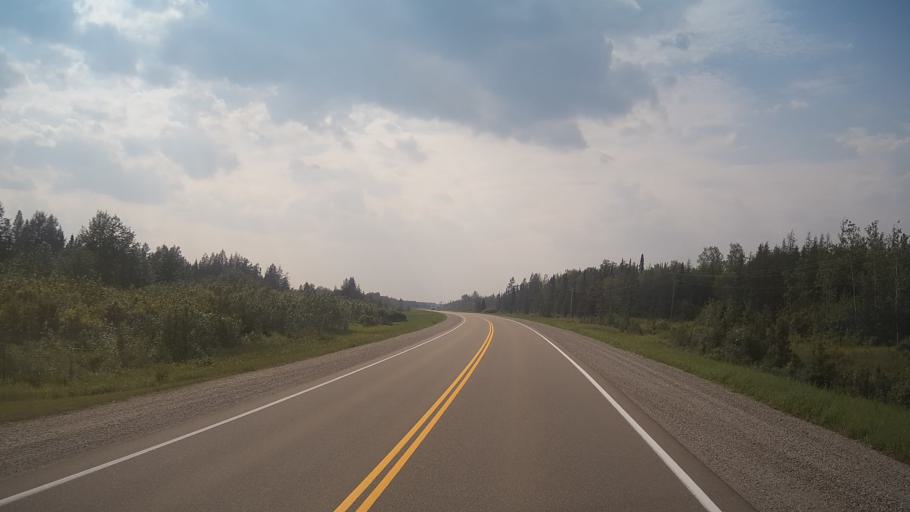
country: CA
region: Ontario
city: Kapuskasing
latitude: 49.5054
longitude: -82.7518
